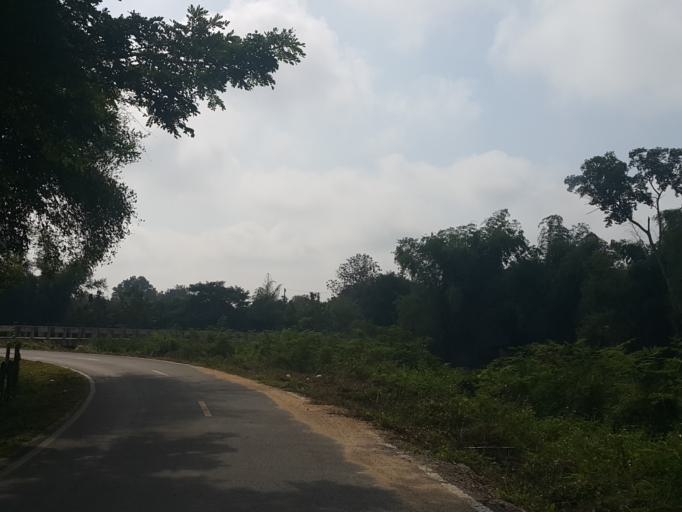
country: TH
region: Lampang
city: Lampang
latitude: 18.3375
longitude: 99.4355
